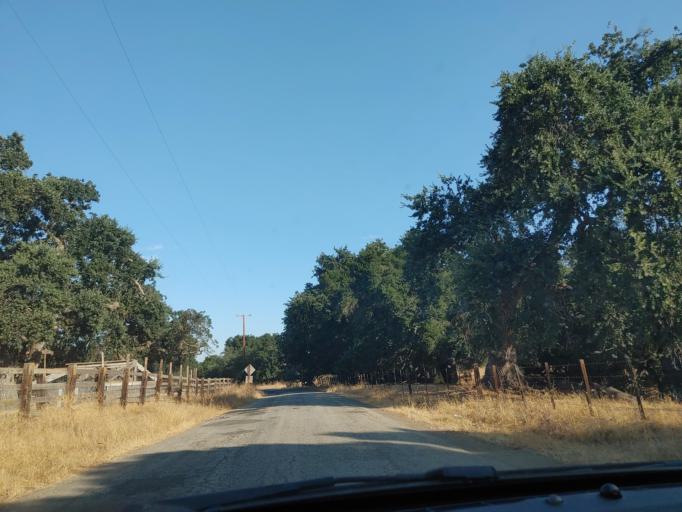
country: US
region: California
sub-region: San Benito County
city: Ridgemark
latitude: 36.7894
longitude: -121.2580
